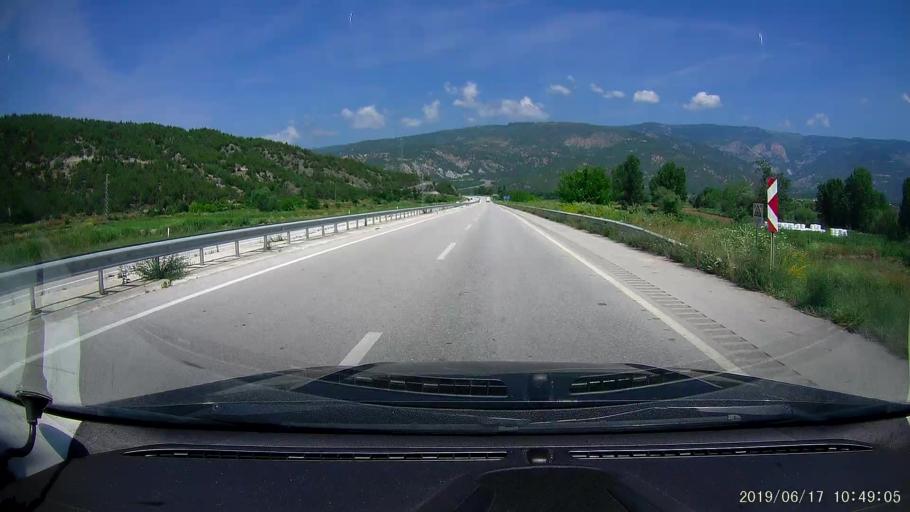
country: TR
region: Corum
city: Hacihamza
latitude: 41.0972
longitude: 34.4177
